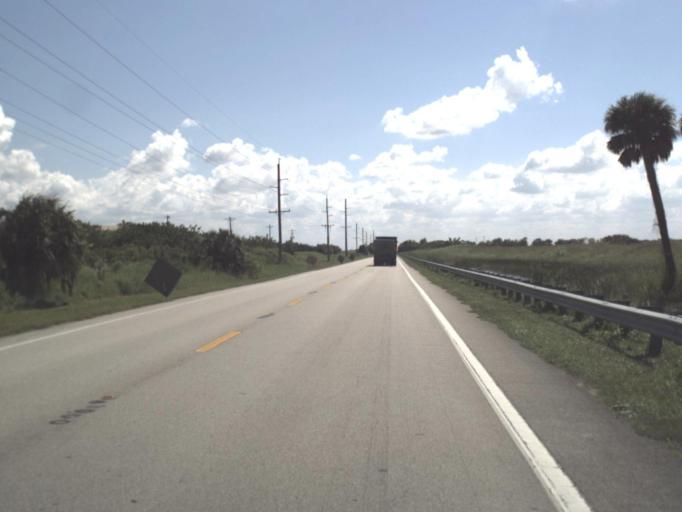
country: US
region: Florida
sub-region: Glades County
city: Moore Haven
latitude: 26.8784
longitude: -81.1226
